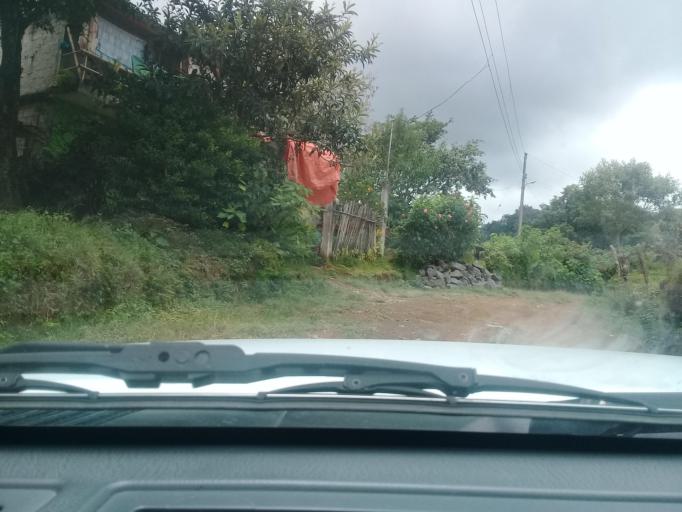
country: MX
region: Veracruz
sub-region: Tlalnelhuayocan
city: Otilpan
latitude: 19.5472
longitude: -96.9760
